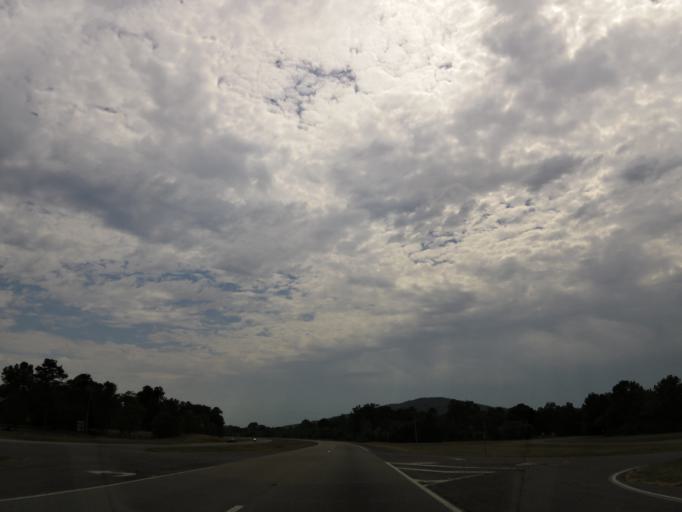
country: US
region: Alabama
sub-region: Jackson County
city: Stevenson
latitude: 34.9032
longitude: -85.8046
